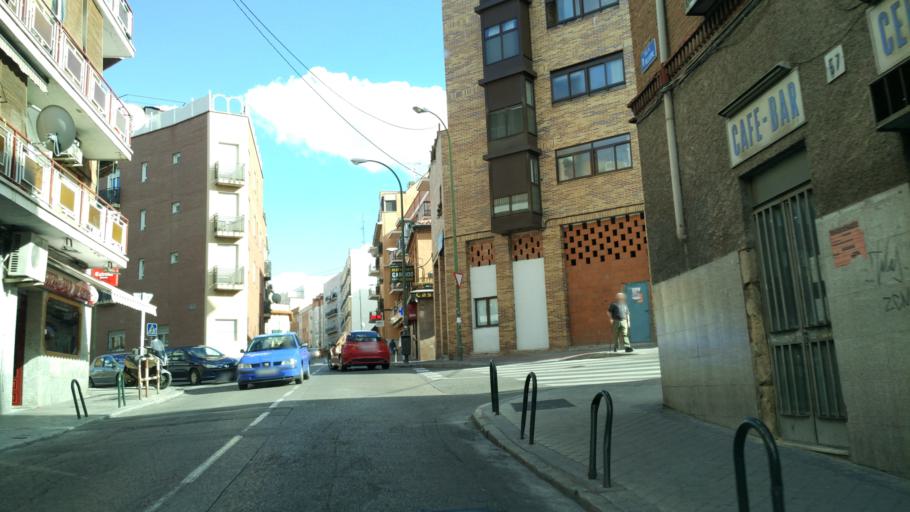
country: ES
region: Madrid
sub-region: Provincia de Madrid
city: Tetuan de las Victorias
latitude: 40.4607
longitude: -3.7080
